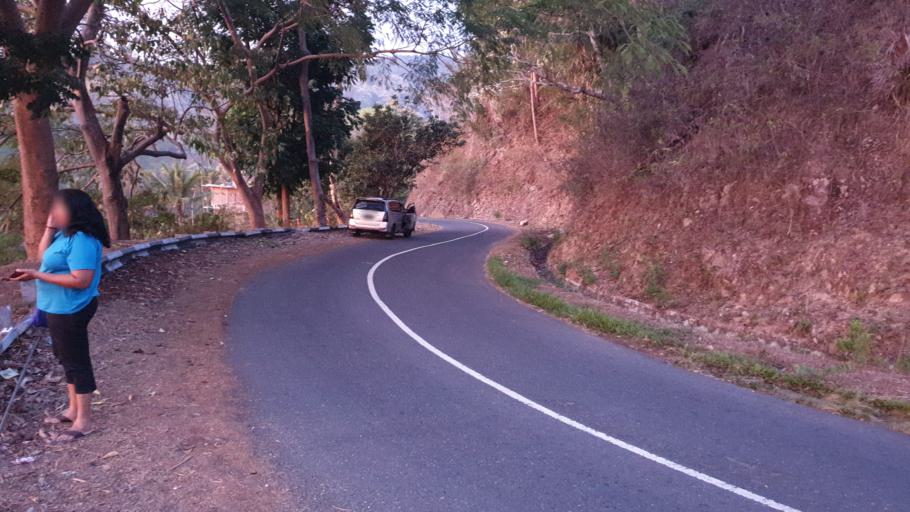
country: ID
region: East Nusa Tenggara
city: Wolowaru
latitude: -8.7888
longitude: 121.9074
